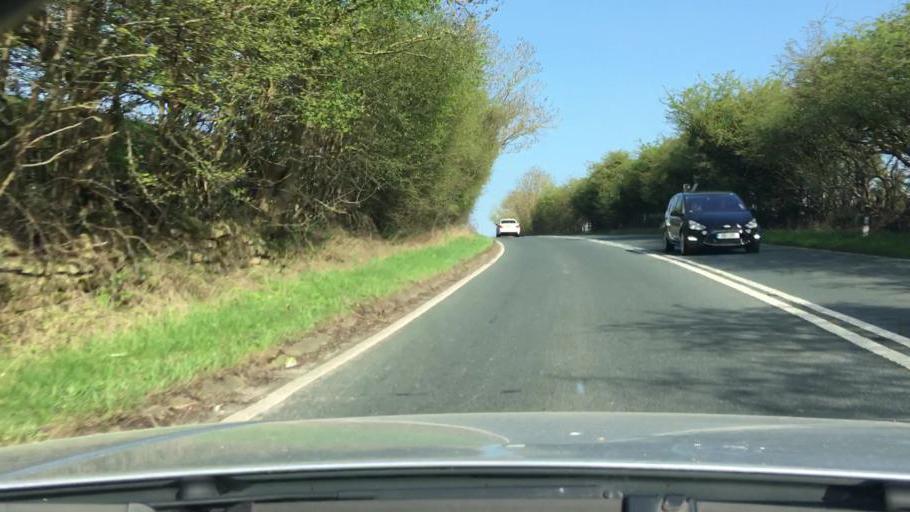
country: GB
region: England
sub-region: North Yorkshire
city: Pannal
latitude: 53.9398
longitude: -1.5365
